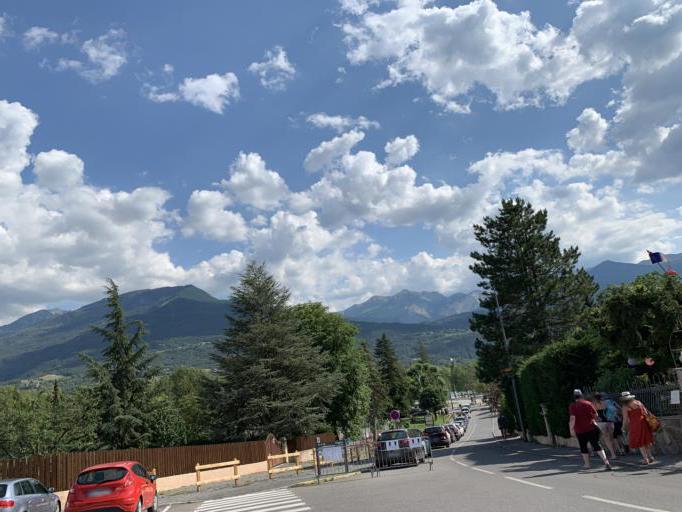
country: FR
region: Provence-Alpes-Cote d'Azur
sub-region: Departement des Hautes-Alpes
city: Embrun
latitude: 44.5520
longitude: 6.4795
